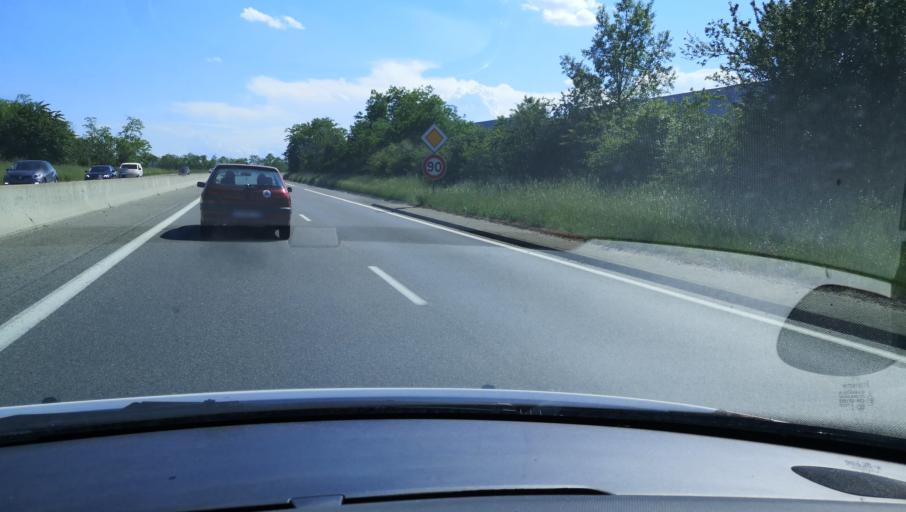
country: FR
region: Rhone-Alpes
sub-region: Departement du Rhone
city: Meyzieu
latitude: 45.7590
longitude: 5.0301
